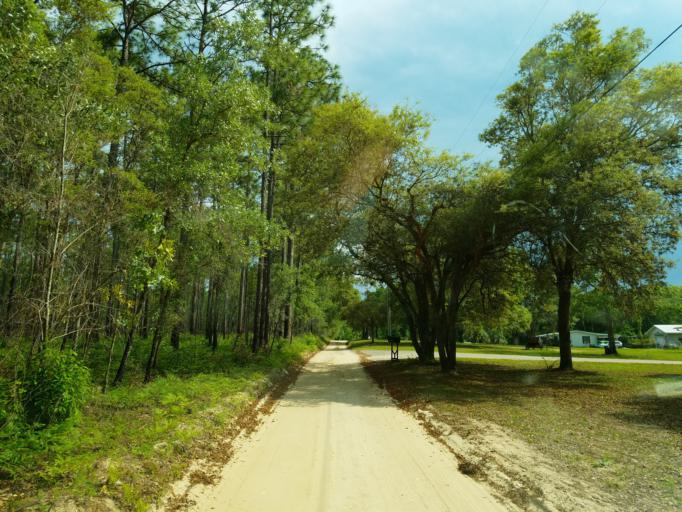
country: US
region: Florida
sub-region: Hernando County
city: Hill 'n Dale
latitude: 28.5553
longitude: -82.2802
